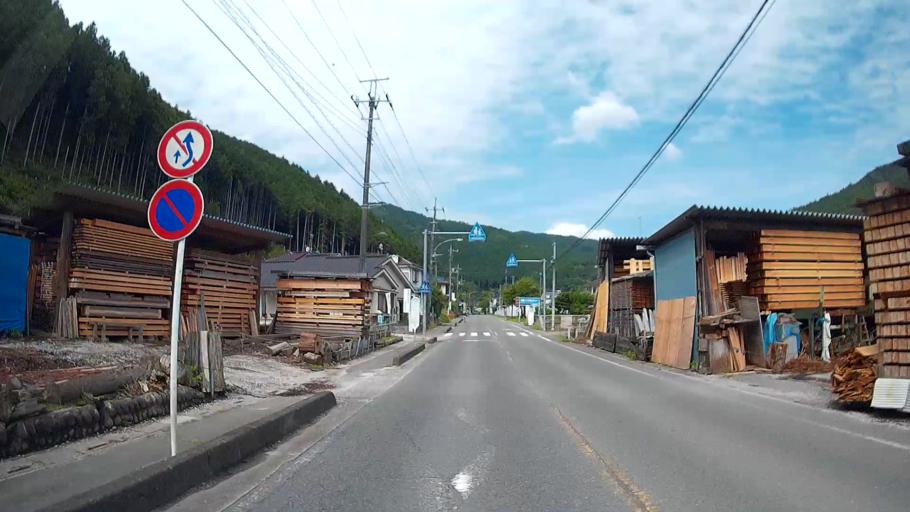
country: JP
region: Saitama
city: Hanno
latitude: 35.8708
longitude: 139.2395
